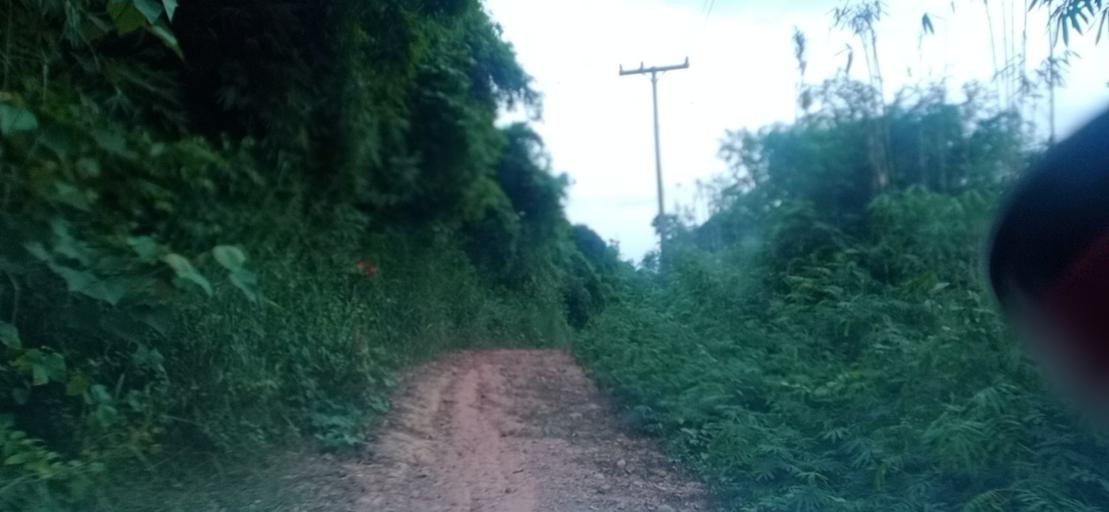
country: TH
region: Changwat Bueng Kan
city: Pak Khat
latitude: 18.5611
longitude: 103.2622
